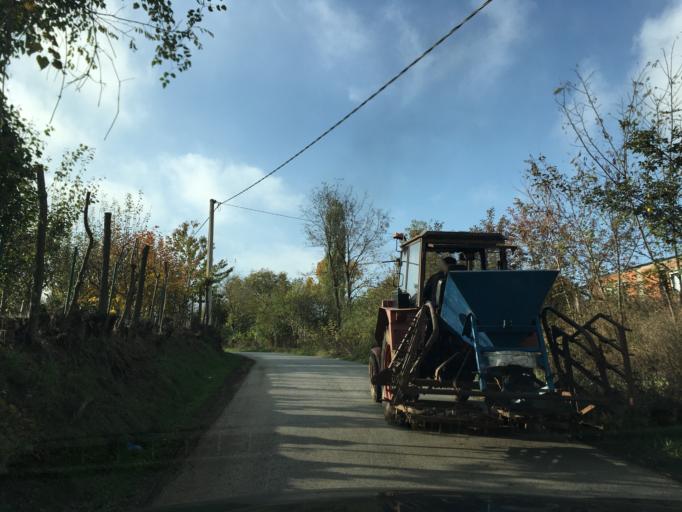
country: RS
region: Central Serbia
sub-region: Belgrade
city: Sopot
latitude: 44.4888
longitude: 20.5683
